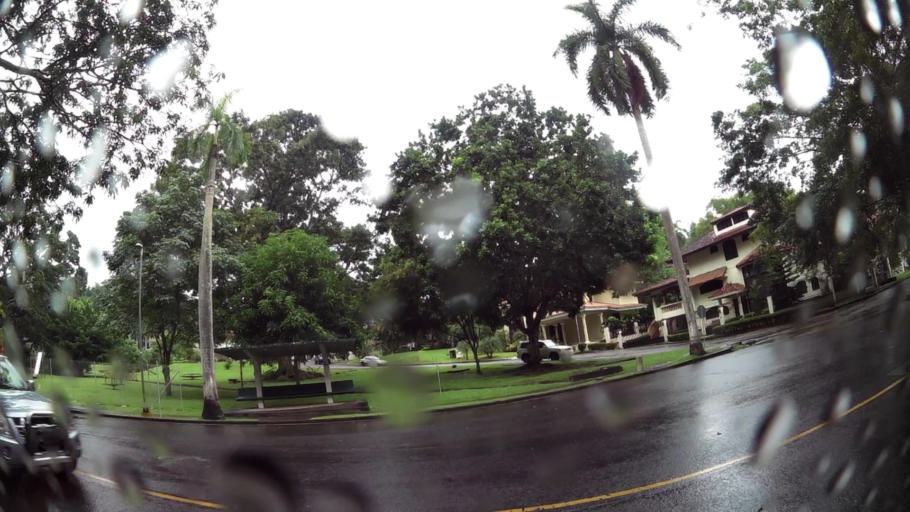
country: PA
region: Panama
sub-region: Distrito de Panama
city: Ancon
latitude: 8.9856
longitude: -79.5576
